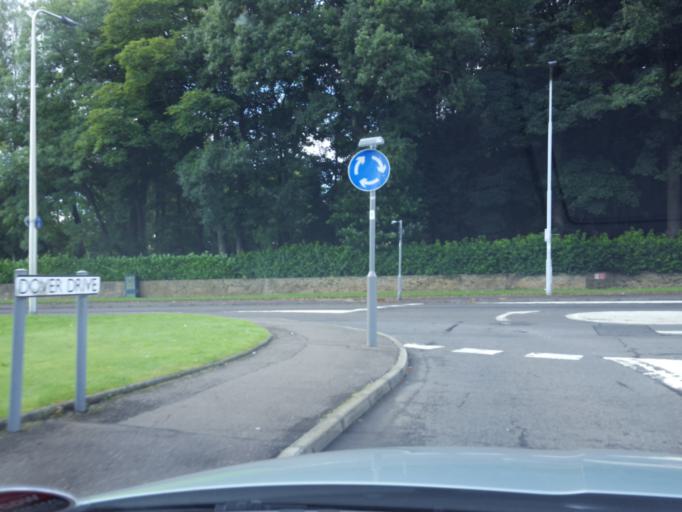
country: GB
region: Scotland
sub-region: Fife
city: Inverkeithing
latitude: 56.0560
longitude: -3.4148
